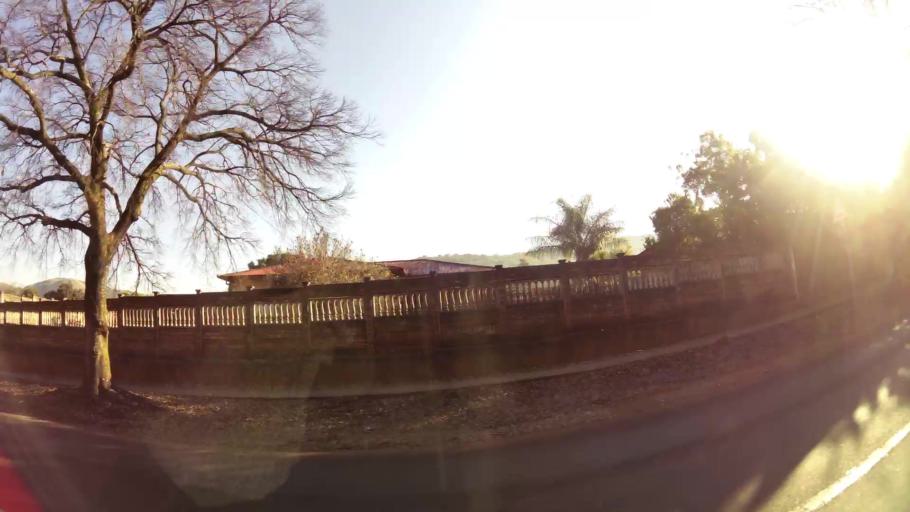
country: ZA
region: Gauteng
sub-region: City of Tshwane Metropolitan Municipality
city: Pretoria
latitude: -25.6998
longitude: 28.1927
